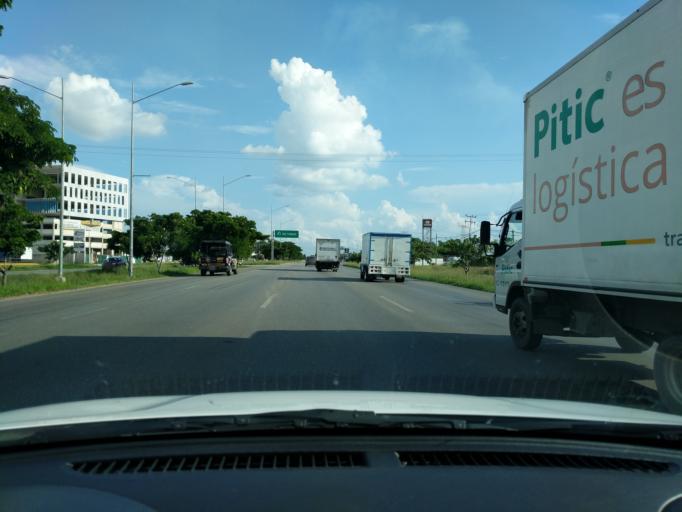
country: MX
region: Yucatan
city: Itzincab Palomeque
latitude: 20.9430
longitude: -89.6991
